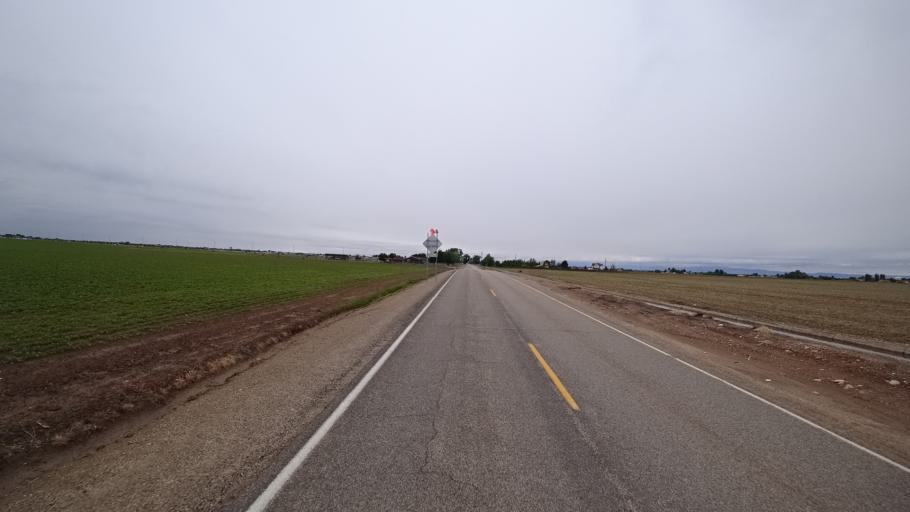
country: US
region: Idaho
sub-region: Ada County
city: Star
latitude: 43.6585
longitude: -116.4734
